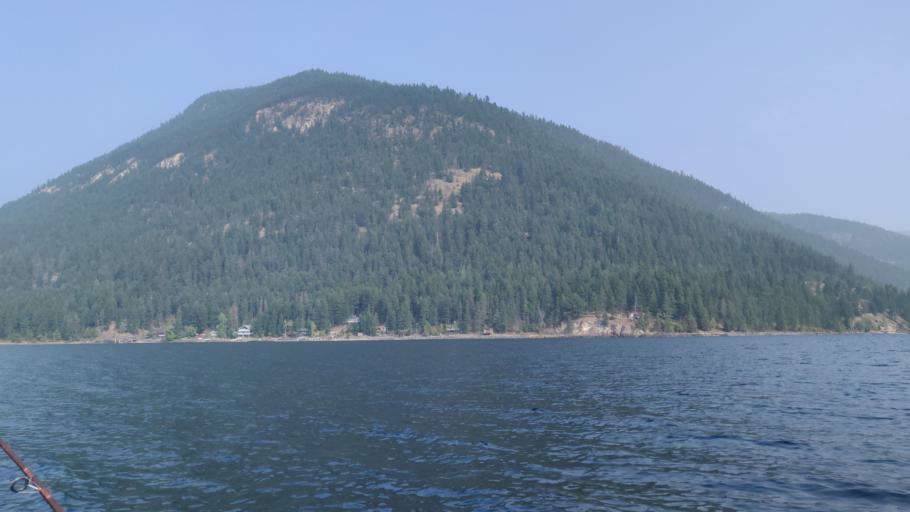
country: CA
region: British Columbia
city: Chase
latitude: 51.0706
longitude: -119.7533
